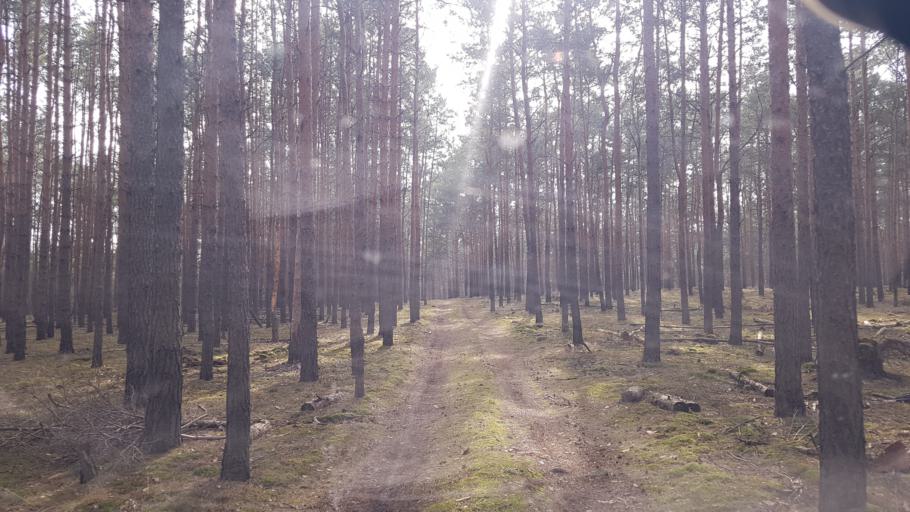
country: DE
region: Brandenburg
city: Schlieben
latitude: 51.6650
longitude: 13.3645
